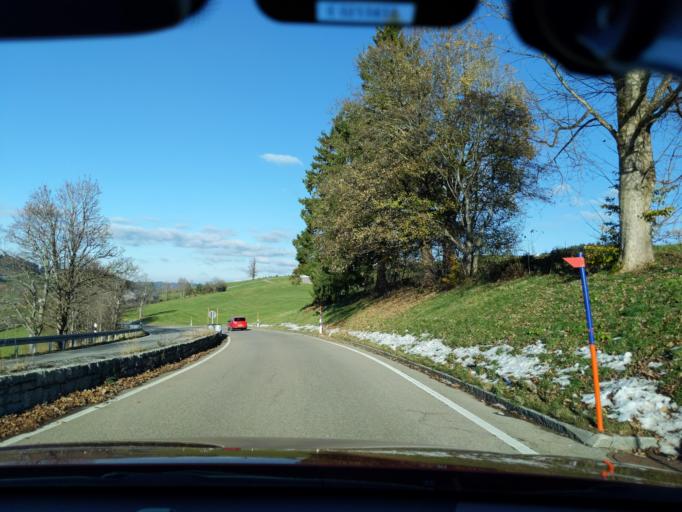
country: DE
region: Bavaria
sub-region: Swabia
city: Oberstaufen
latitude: 47.5436
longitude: 9.9887
